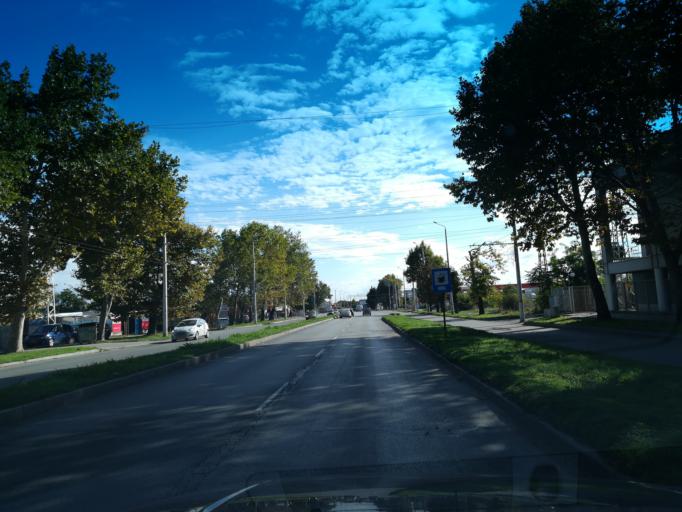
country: BG
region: Stara Zagora
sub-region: Obshtina Stara Zagora
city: Stara Zagora
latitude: 42.4060
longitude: 25.6412
